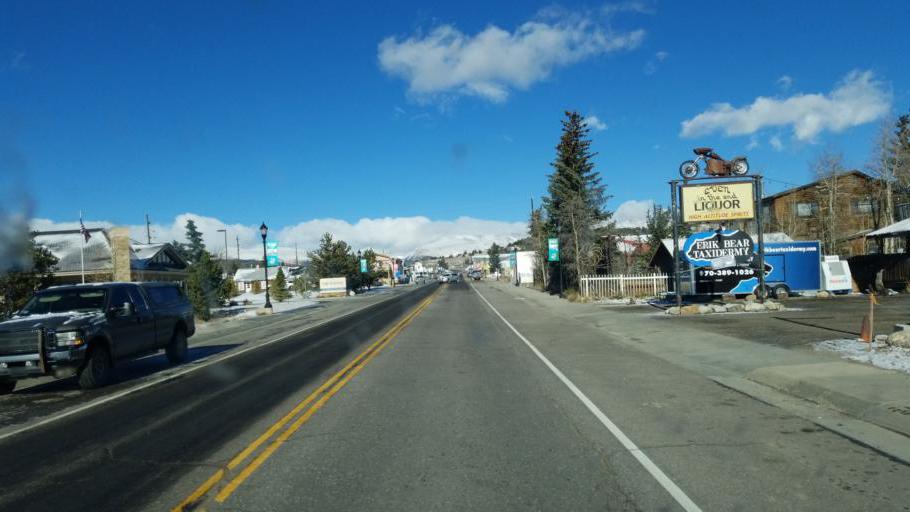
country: US
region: Colorado
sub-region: Park County
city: Fairplay
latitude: 39.2218
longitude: -105.9967
